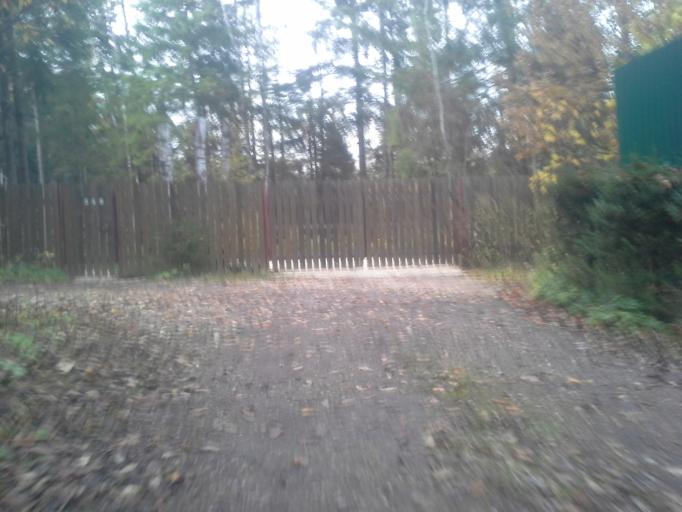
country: RU
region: Moskovskaya
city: Krasnoznamensk
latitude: 55.5818
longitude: 37.0205
